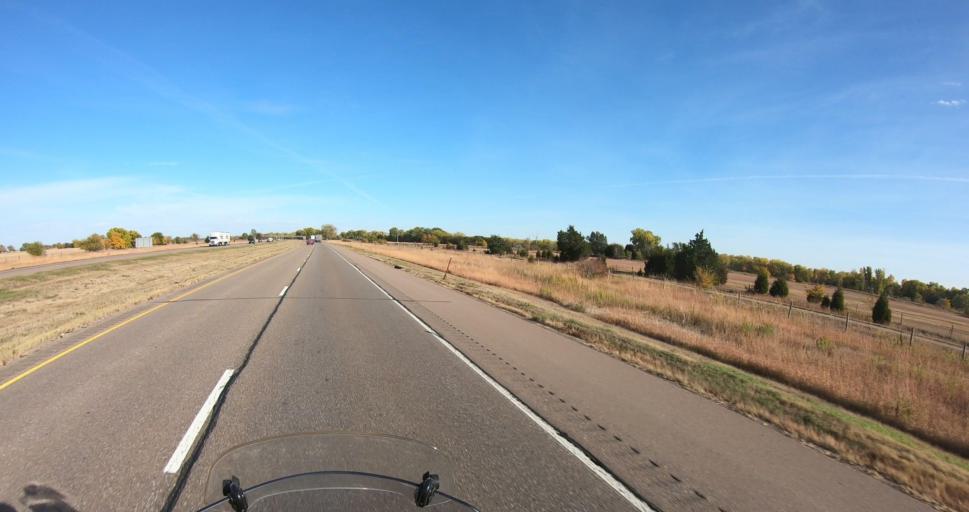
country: US
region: Nebraska
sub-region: Buffalo County
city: Shelton
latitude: 40.7223
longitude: -98.7128
